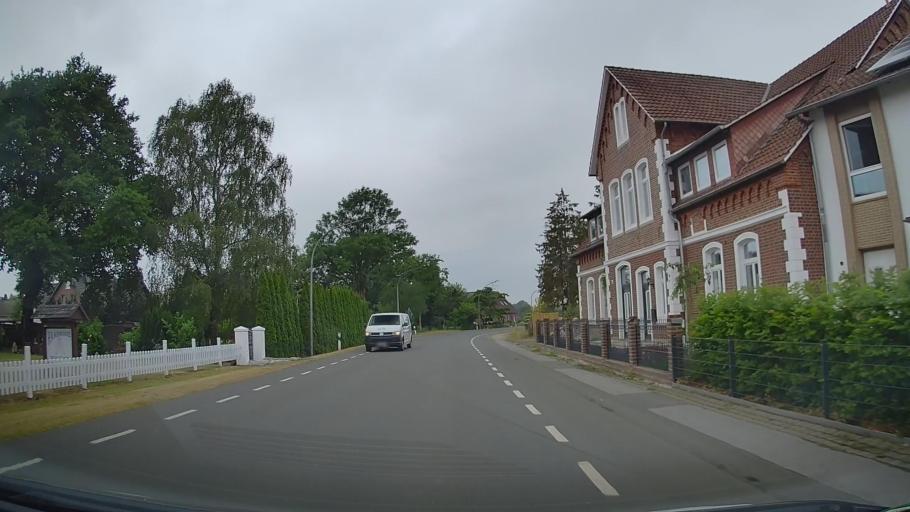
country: DE
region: Lower Saxony
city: Brockum
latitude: 52.4629
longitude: 8.5152
